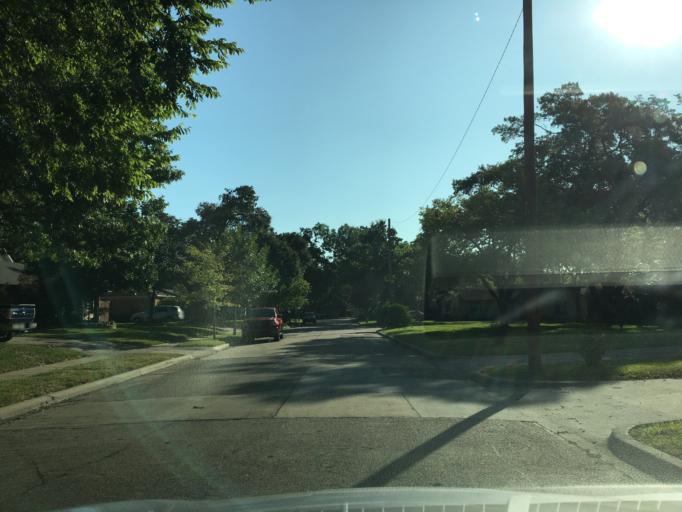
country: US
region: Texas
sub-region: Dallas County
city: Highland Park
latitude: 32.8525
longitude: -96.7137
